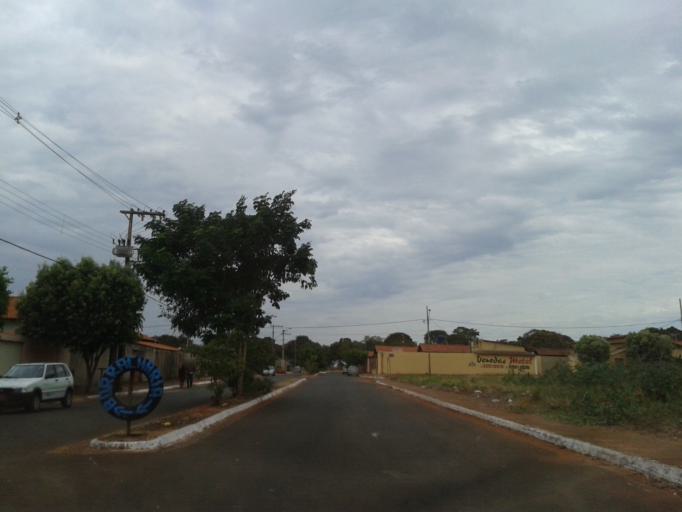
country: BR
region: Minas Gerais
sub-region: Santa Vitoria
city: Santa Vitoria
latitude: -18.8541
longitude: -50.1197
